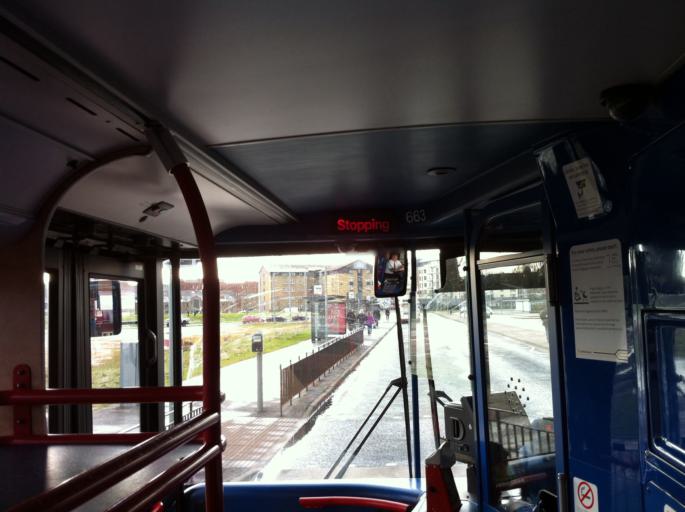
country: GB
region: Scotland
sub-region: West Lothian
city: Seafield
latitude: 55.9805
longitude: -3.1769
